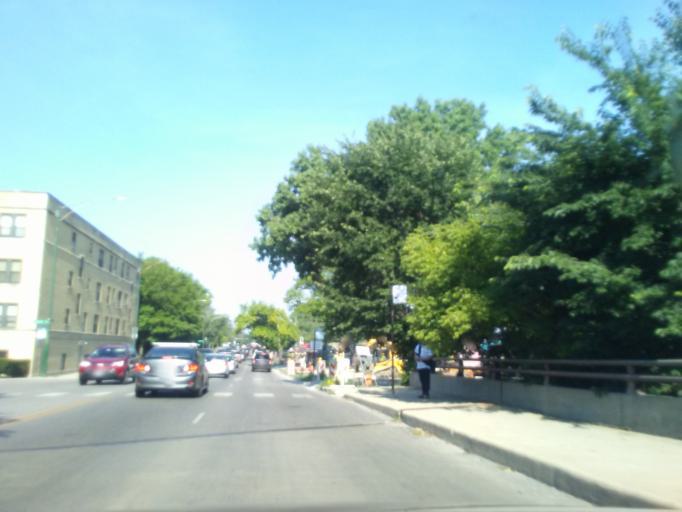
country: US
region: Illinois
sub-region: Cook County
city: Lincolnwood
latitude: 41.9756
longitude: -87.7243
